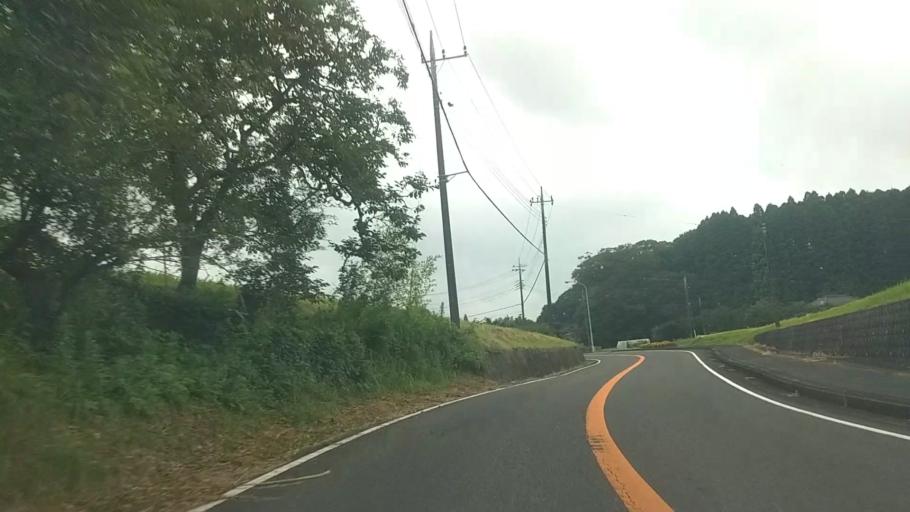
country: JP
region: Chiba
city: Kawaguchi
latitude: 35.2450
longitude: 140.0784
